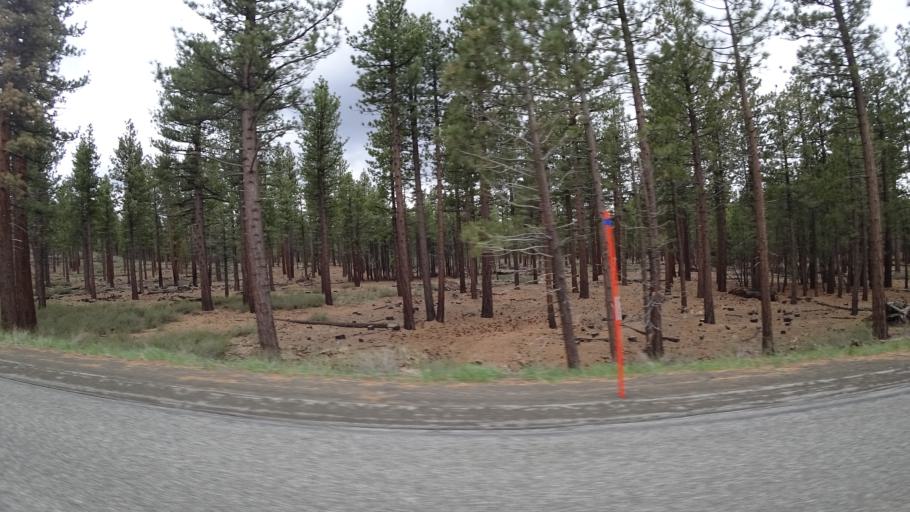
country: US
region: California
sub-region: Mono County
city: Mammoth Lakes
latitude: 37.7262
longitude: -118.9644
